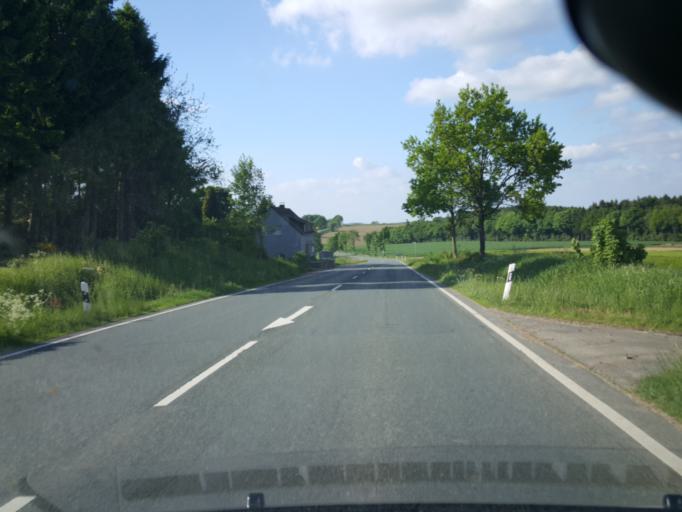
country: DE
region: North Rhine-Westphalia
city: Halver
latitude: 51.2112
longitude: 7.4877
